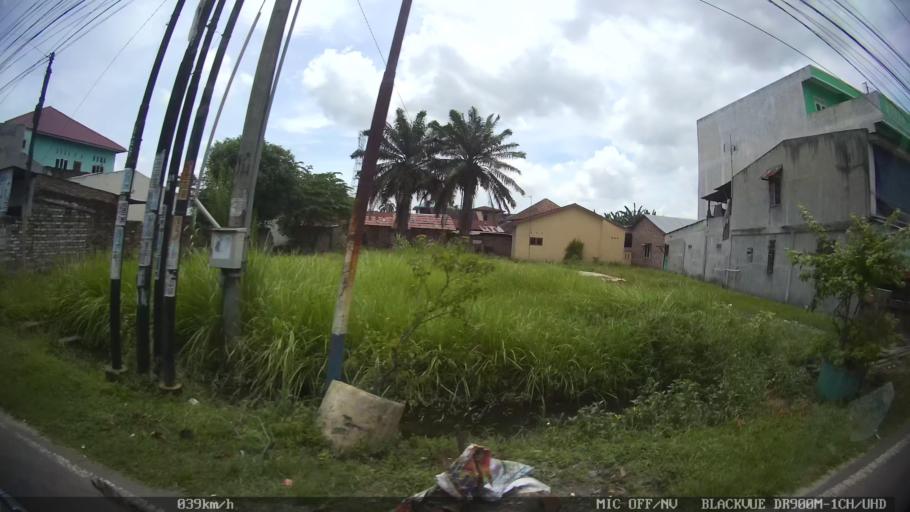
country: ID
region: North Sumatra
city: Percut
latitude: 3.5619
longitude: 98.8809
